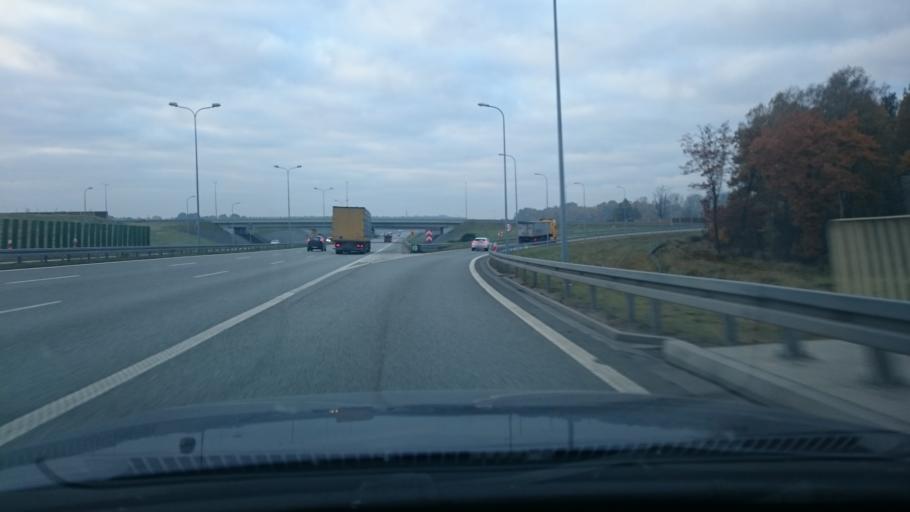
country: PL
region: Silesian Voivodeship
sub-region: Powiat rybnicki
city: Stanowice
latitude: 50.1341
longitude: 18.6919
